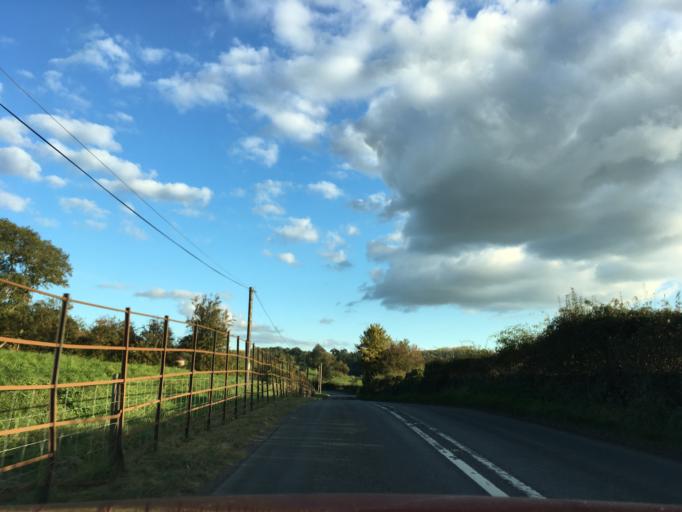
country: GB
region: England
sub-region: Herefordshire
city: Ledbury
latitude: 52.0314
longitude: -2.3820
